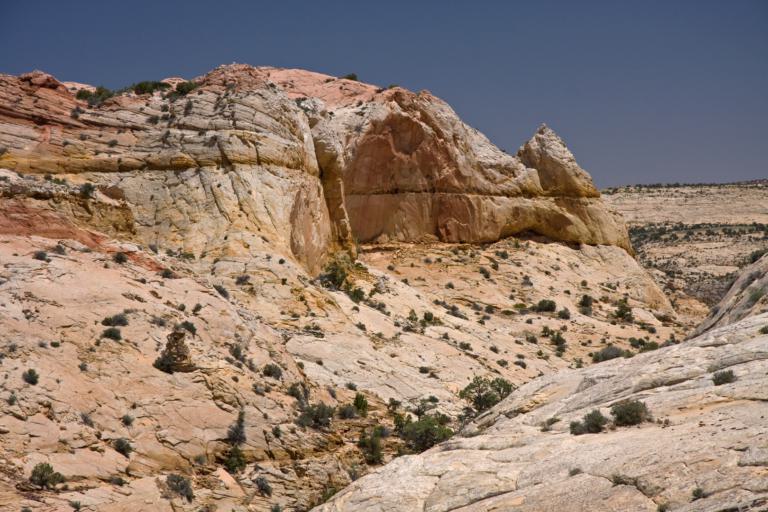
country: US
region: Utah
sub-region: Wayne County
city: Loa
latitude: 37.7496
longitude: -111.4432
